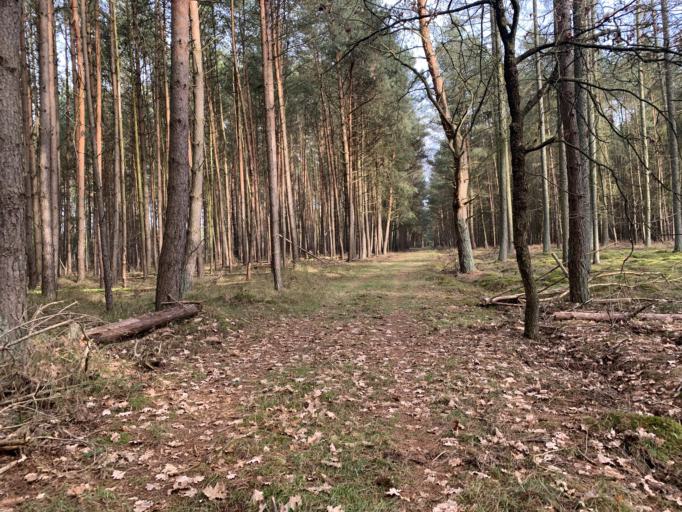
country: DE
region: Mecklenburg-Vorpommern
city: Wesenberg
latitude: 53.2848
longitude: 12.8700
